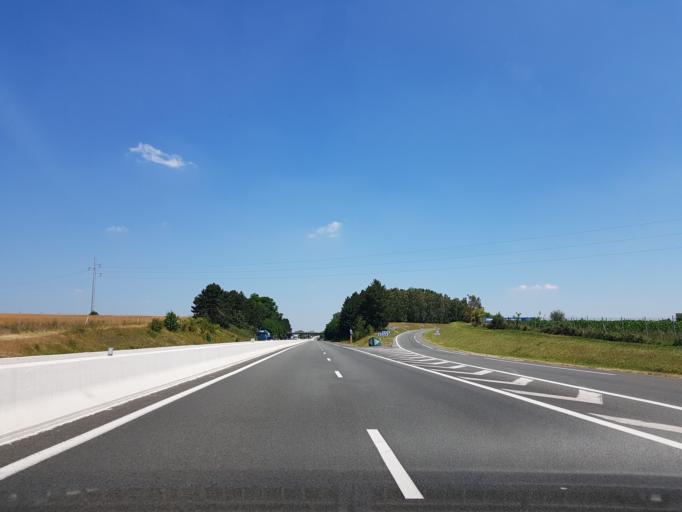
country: FR
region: Nord-Pas-de-Calais
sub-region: Departement du Nord
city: Raillencourt-Sainte-Olle
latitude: 50.1743
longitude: 3.1826
